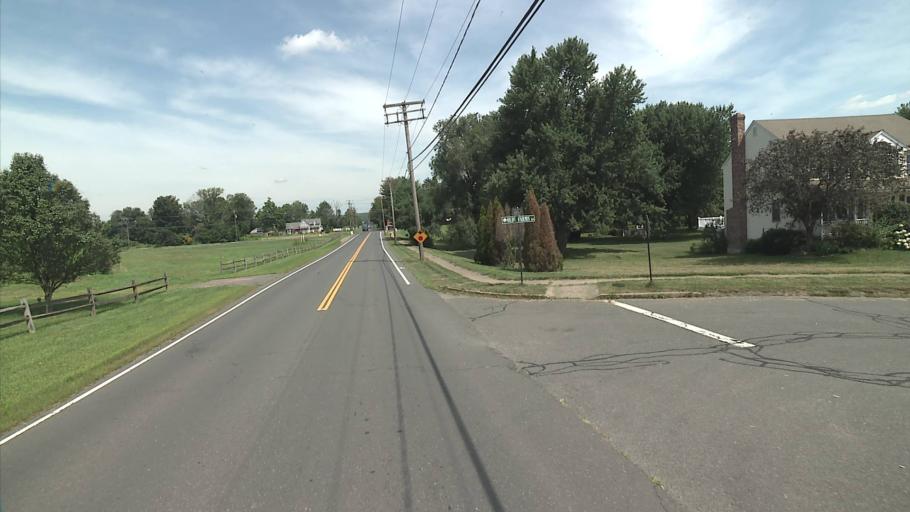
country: US
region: Connecticut
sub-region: Tolland County
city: Ellington
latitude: 41.9015
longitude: -72.4781
